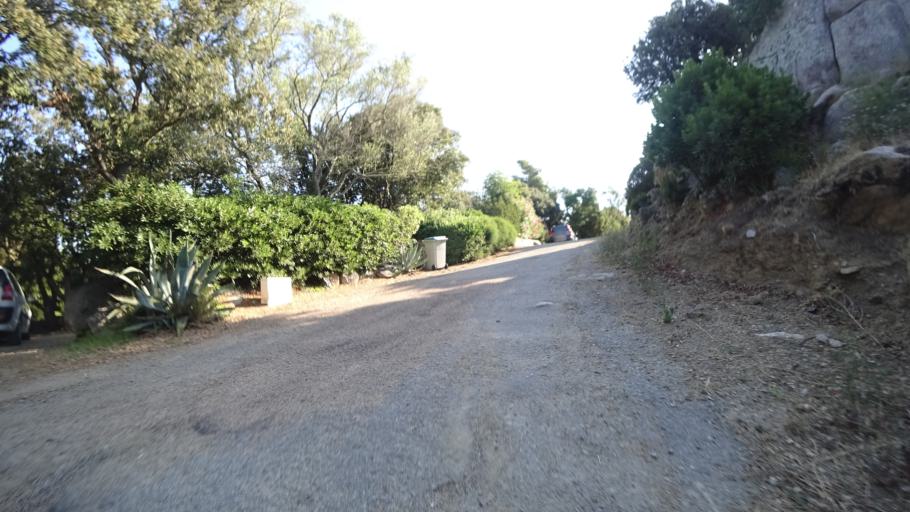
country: FR
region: Corsica
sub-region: Departement de la Corse-du-Sud
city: Porto-Vecchio
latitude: 41.6218
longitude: 9.3408
